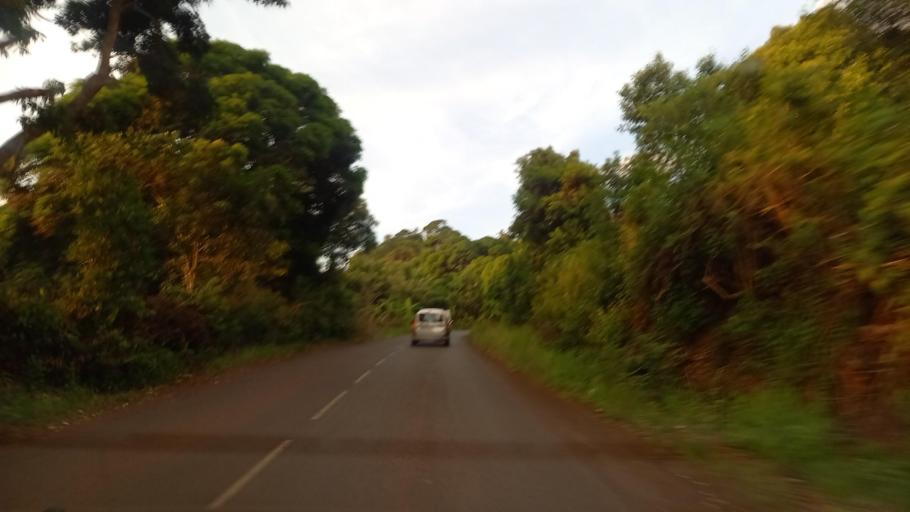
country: YT
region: M'Tsangamouji
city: M'Tsangamouji
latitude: -12.7529
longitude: 45.0904
